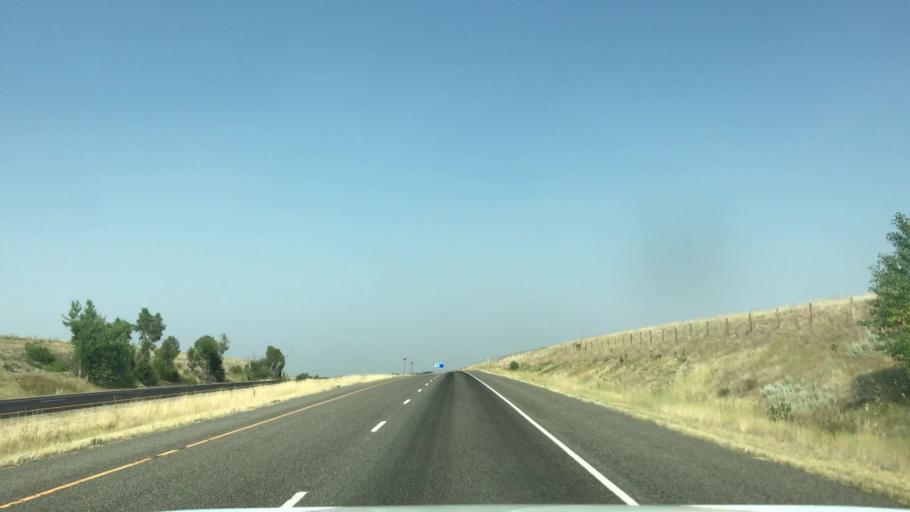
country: US
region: Montana
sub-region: Cascade County
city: Sun Prairie
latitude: 47.2469
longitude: -111.7162
